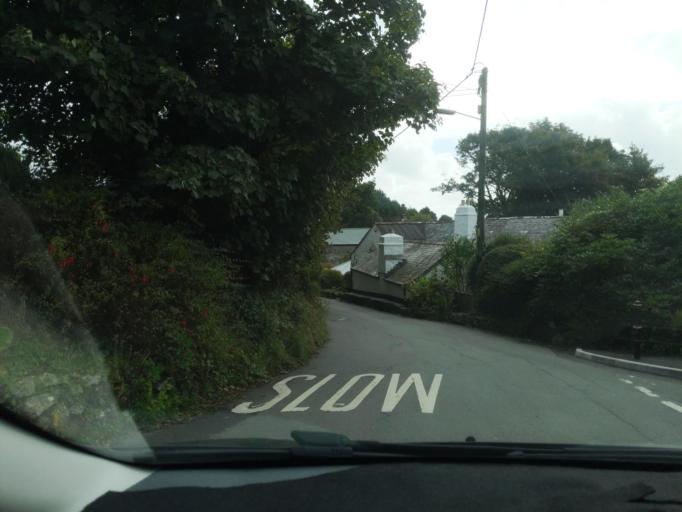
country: GB
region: England
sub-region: Cornwall
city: Lostwithiel
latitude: 50.4001
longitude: -4.7038
